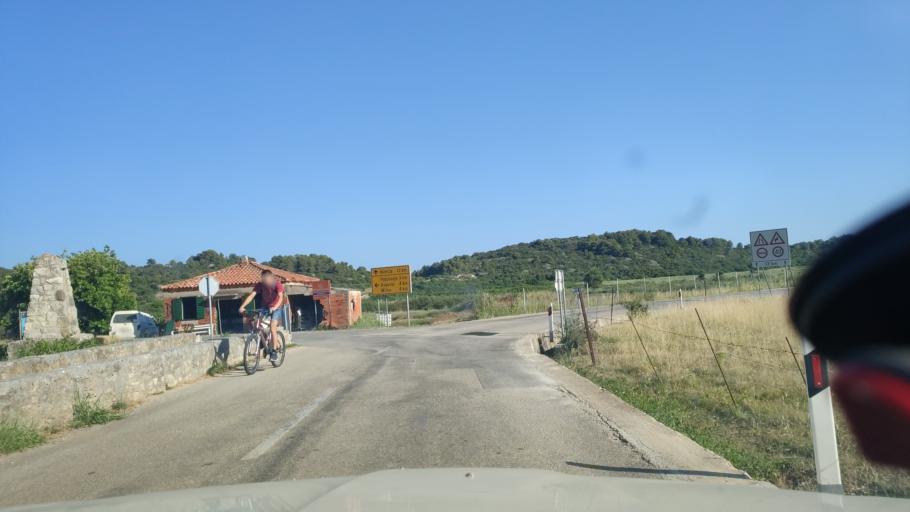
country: HR
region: Splitsko-Dalmatinska
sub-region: Grad Vis
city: Vis
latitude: 43.0424
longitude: 16.1981
